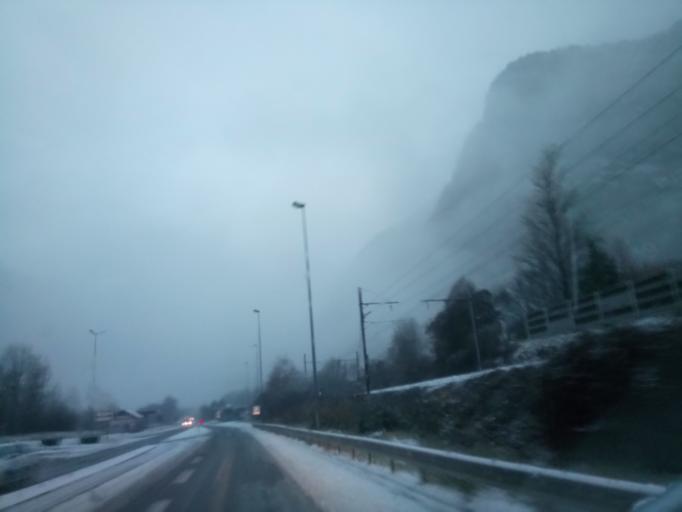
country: FR
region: Rhone-Alpes
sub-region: Departement de la Savoie
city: Saint-Jean-de-Maurienne
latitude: 45.3142
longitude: 6.3367
